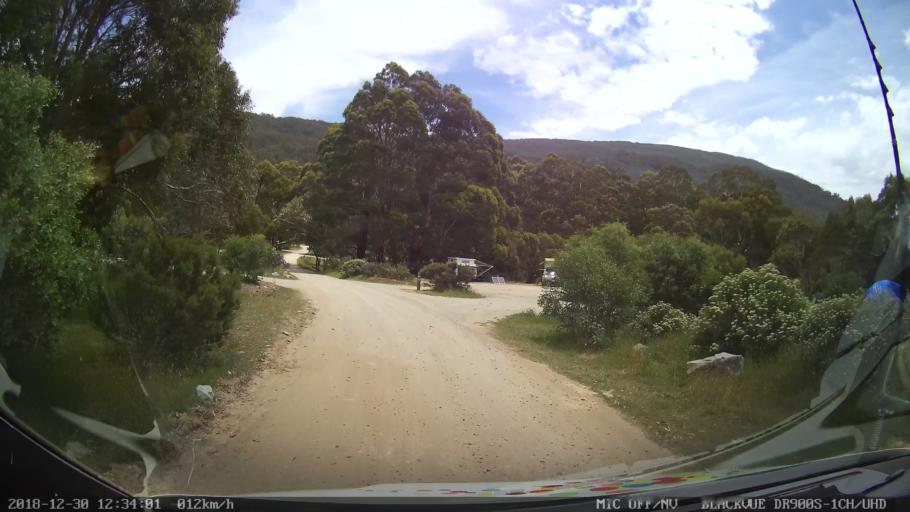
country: AU
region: New South Wales
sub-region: Snowy River
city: Jindabyne
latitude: -36.3223
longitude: 148.4664
